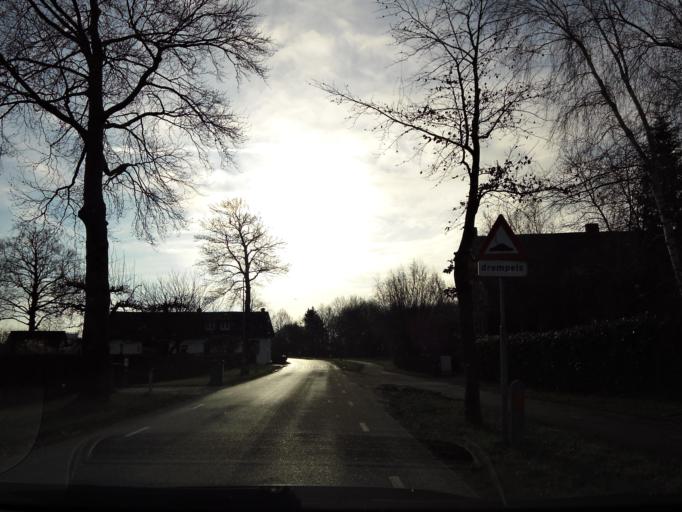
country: NL
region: Limburg
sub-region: Gemeente Beesel
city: Beesel
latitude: 51.2439
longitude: 6.0320
